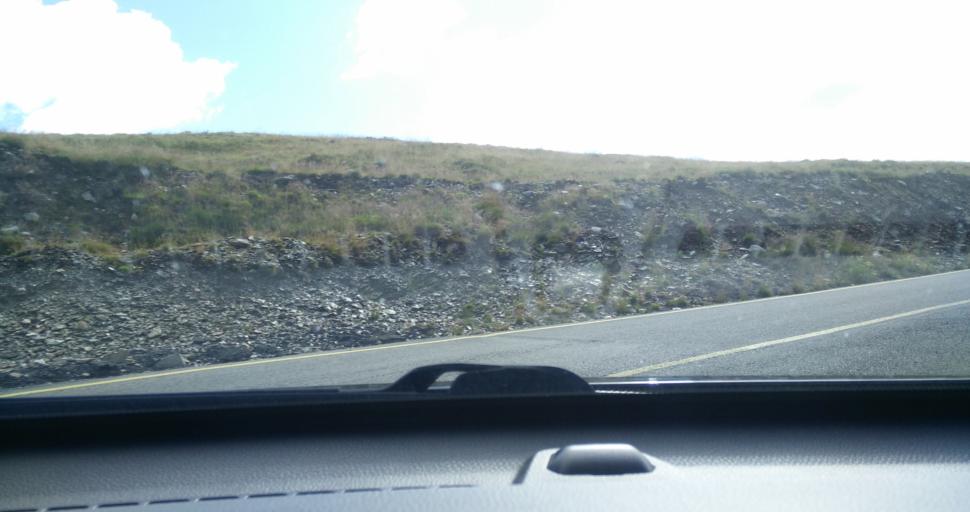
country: RO
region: Gorj
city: Novaci-Straini
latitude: 45.3194
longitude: 23.6822
